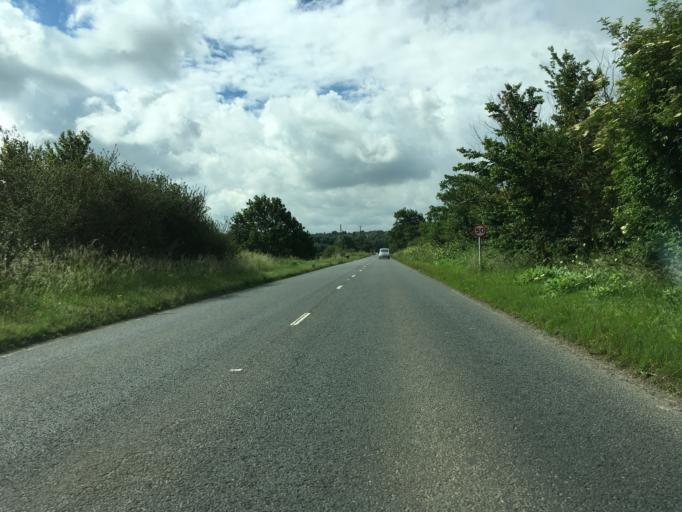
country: GB
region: England
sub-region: Borough of Swindon
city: Highworth
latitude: 51.6472
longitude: -1.7083
